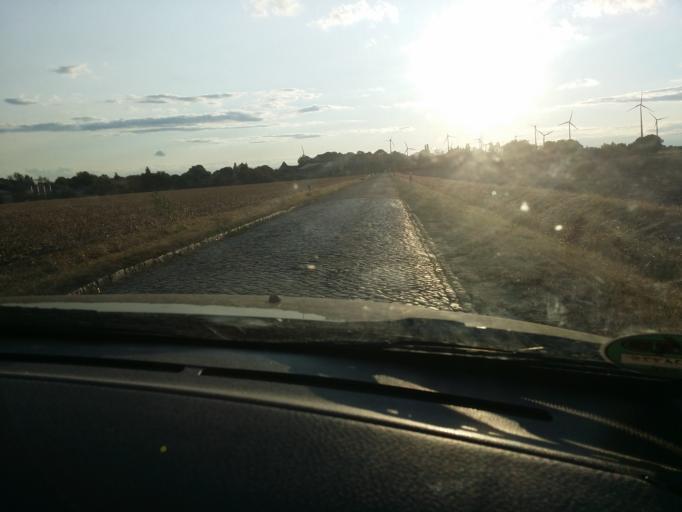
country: DE
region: Saxony-Anhalt
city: Nauendorf
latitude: 51.6142
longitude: 11.8957
